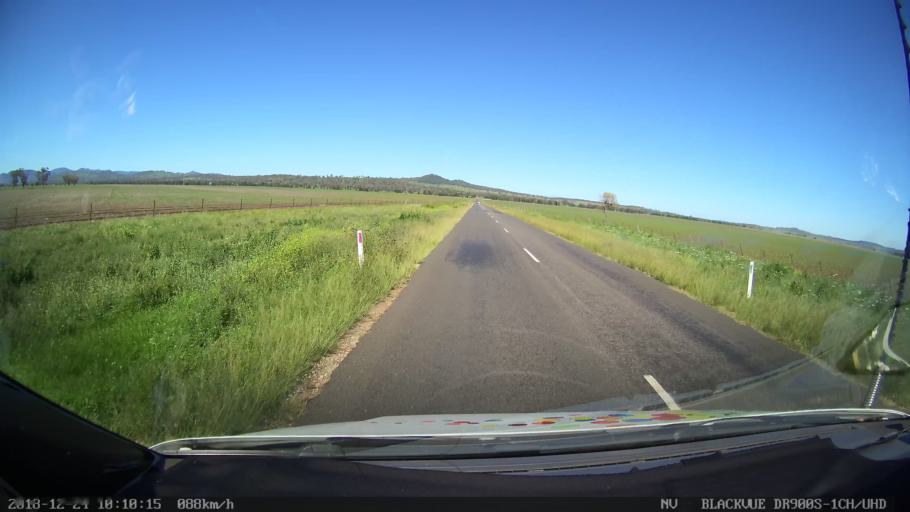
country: AU
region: New South Wales
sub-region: Liverpool Plains
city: Quirindi
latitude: -31.6670
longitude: 150.6785
